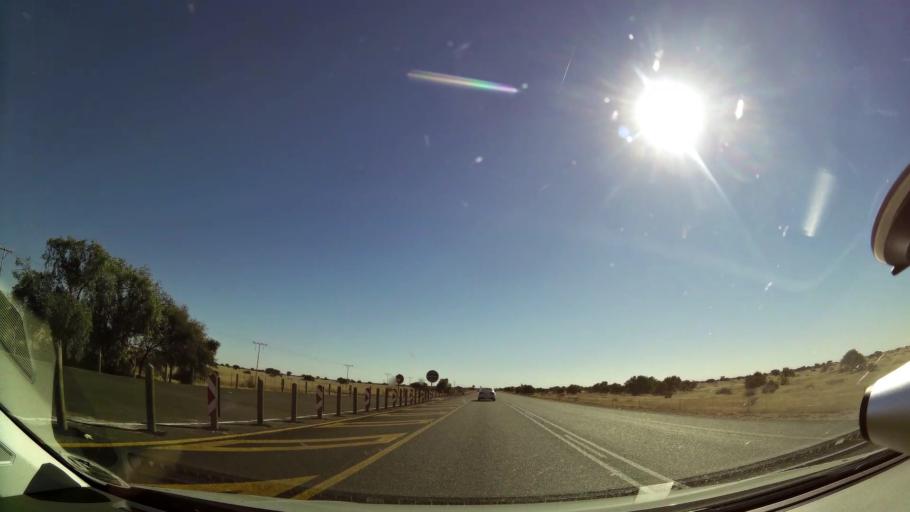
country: ZA
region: Northern Cape
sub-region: Frances Baard District Municipality
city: Warrenton
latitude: -28.1557
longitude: 24.8393
